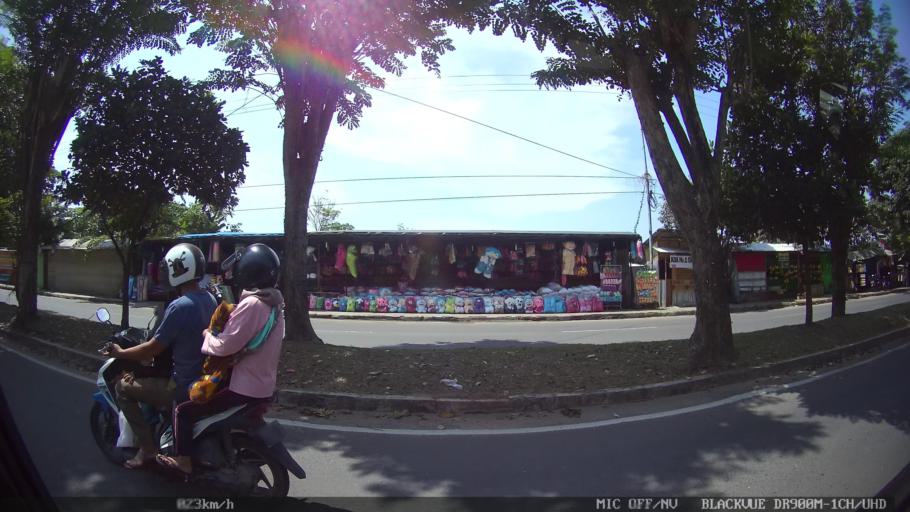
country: ID
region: Lampung
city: Kedaton
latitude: -5.3828
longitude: 105.2789
